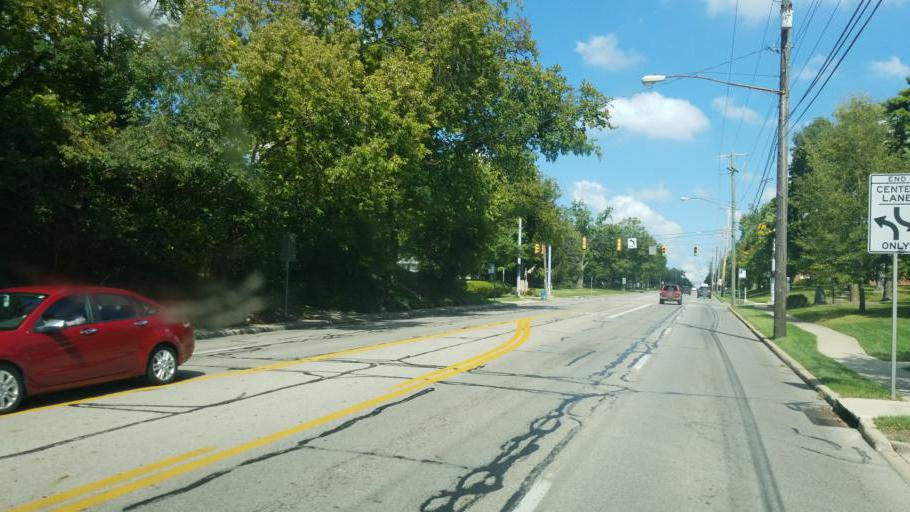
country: US
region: Ohio
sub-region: Franklin County
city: Worthington
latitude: 40.0799
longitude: -83.0185
